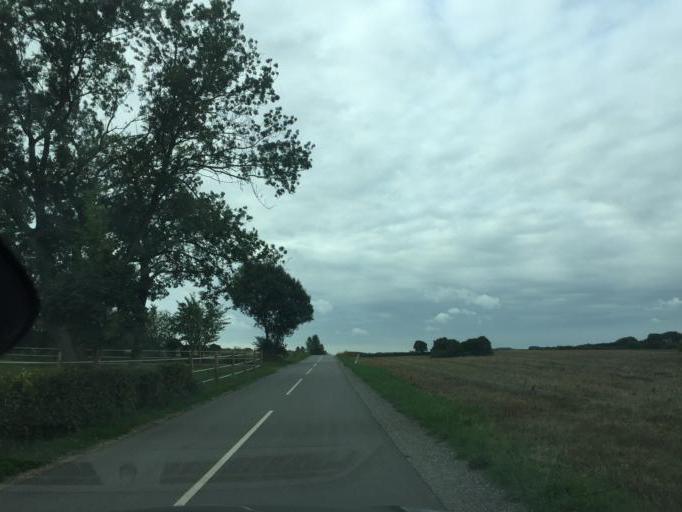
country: DK
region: South Denmark
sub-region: Assens Kommune
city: Tommerup Stationsby
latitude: 55.3727
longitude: 10.1696
